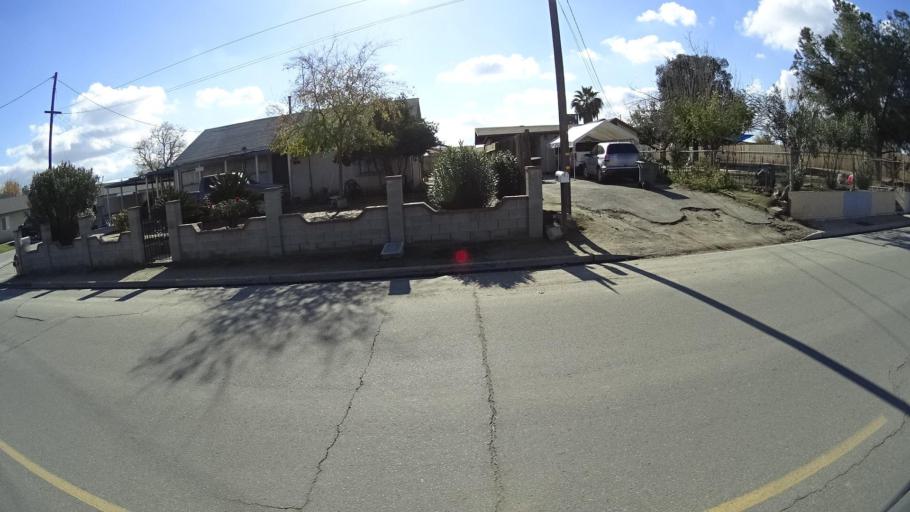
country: US
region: California
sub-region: Kern County
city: McFarland
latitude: 35.6744
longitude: -119.2392
